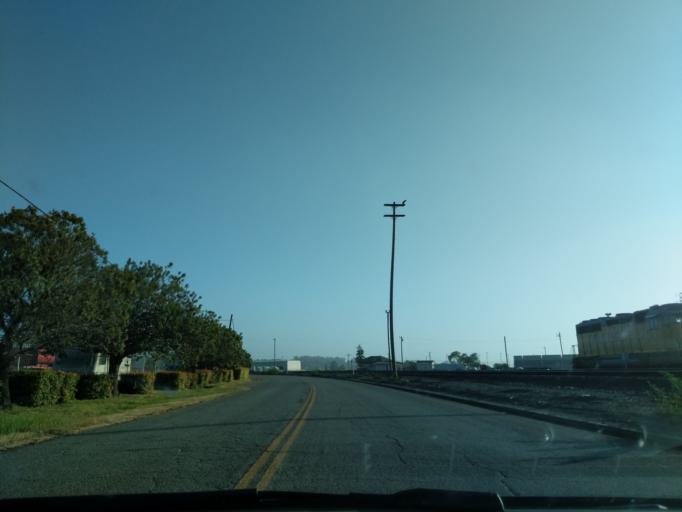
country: US
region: California
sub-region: Monterey County
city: Pajaro
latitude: 36.8943
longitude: -121.7449
